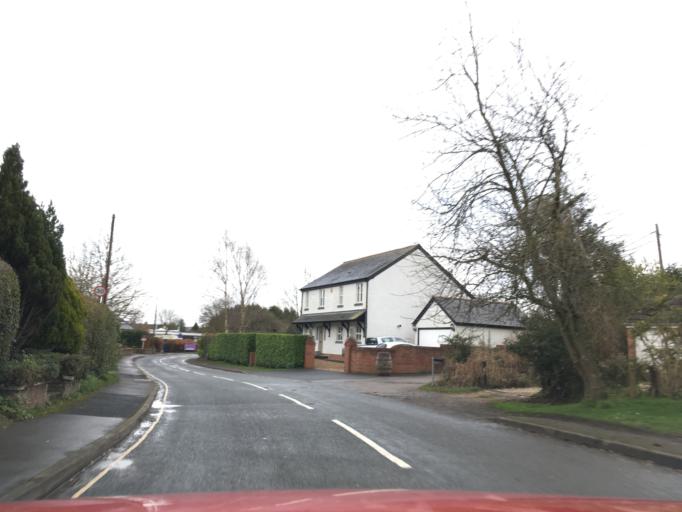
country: GB
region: England
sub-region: Worcestershire
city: Evesham
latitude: 52.0434
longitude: -1.9733
